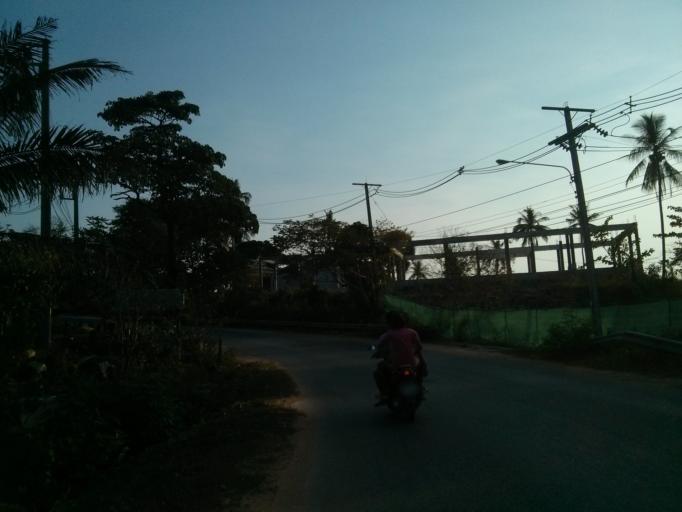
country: TH
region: Krabi
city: Saladan
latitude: 7.5605
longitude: 99.0386
